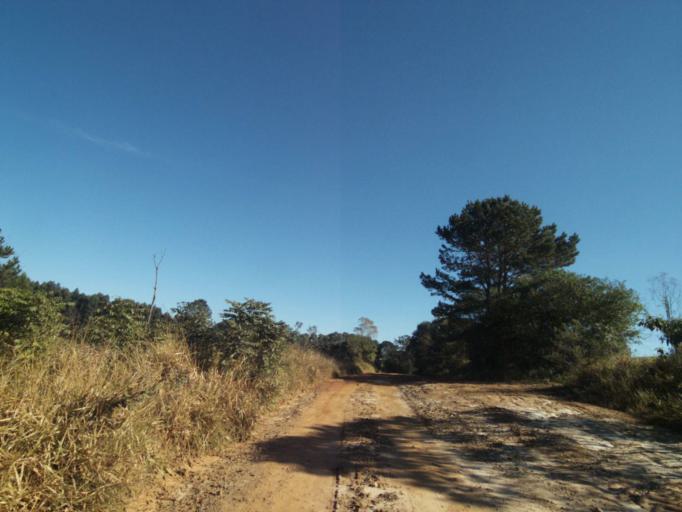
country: BR
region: Parana
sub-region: Tibagi
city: Tibagi
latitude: -24.5368
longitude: -50.3701
